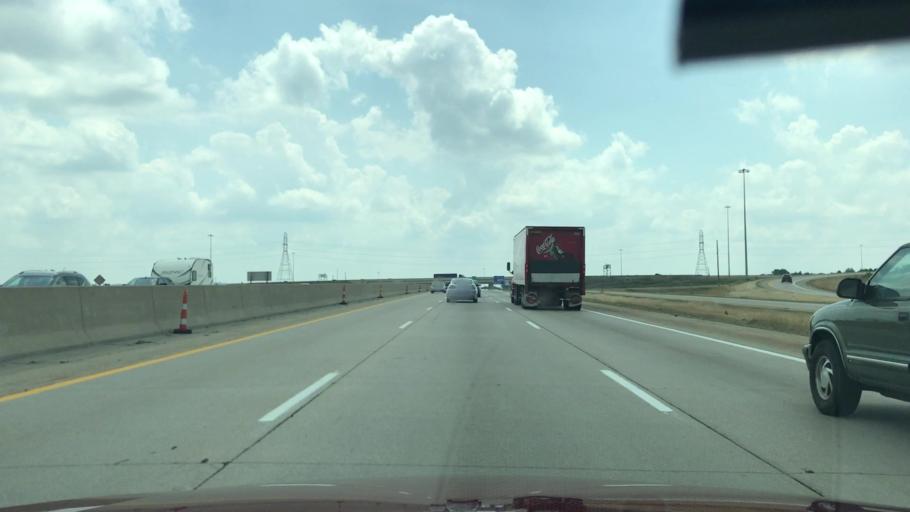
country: US
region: Michigan
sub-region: Kent County
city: Cutlerville
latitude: 42.8544
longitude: -85.6790
